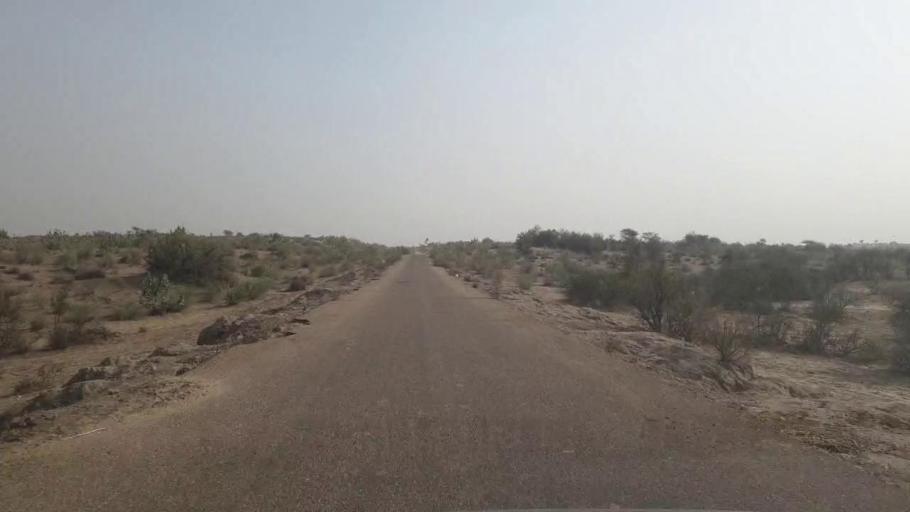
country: PK
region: Sindh
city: Chor
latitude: 25.4985
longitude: 69.9700
